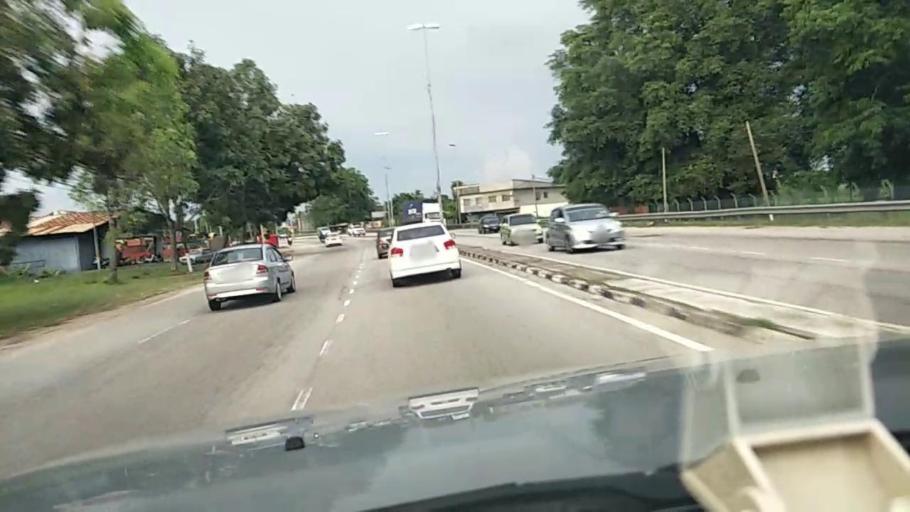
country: MY
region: Perak
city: Kampong Dungun
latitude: 3.1294
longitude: 101.3742
